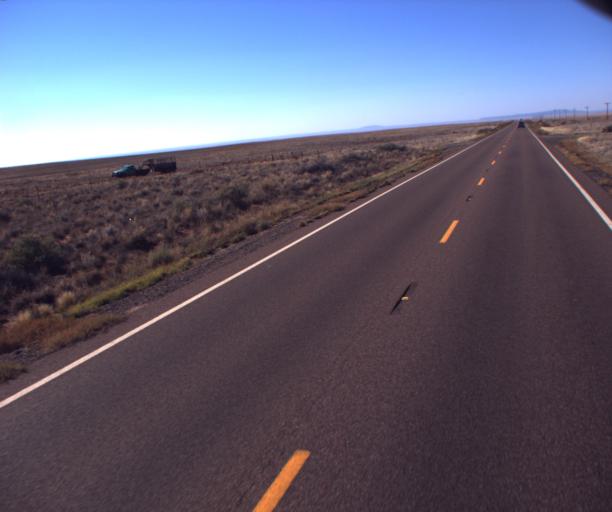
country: US
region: Arizona
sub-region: Navajo County
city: Winslow
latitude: 35.1128
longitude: -110.5190
